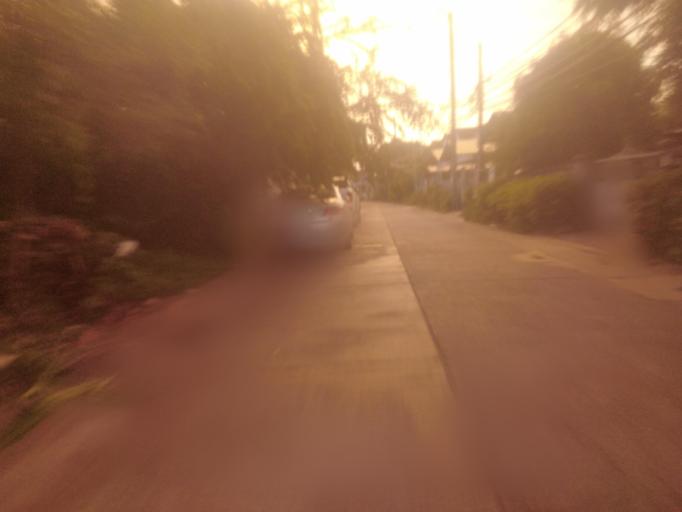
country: TH
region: Bangkok
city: Phasi Charoen
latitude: 13.7445
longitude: 100.4449
